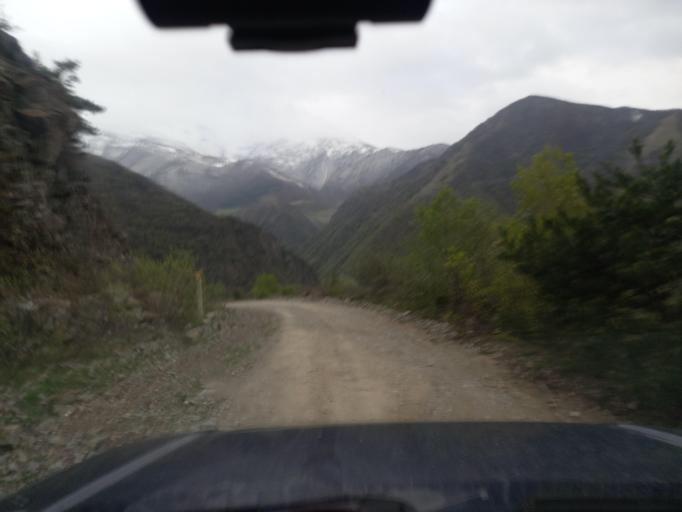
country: RU
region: North Ossetia
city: Mizur
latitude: 42.8523
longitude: 44.1637
